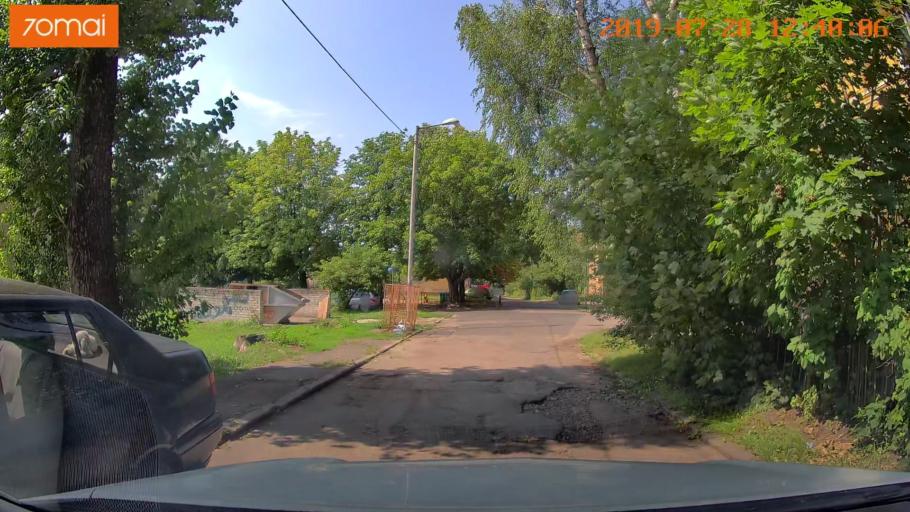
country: RU
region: Kaliningrad
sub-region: Gorod Kaliningrad
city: Kaliningrad
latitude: 54.7111
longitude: 20.4518
